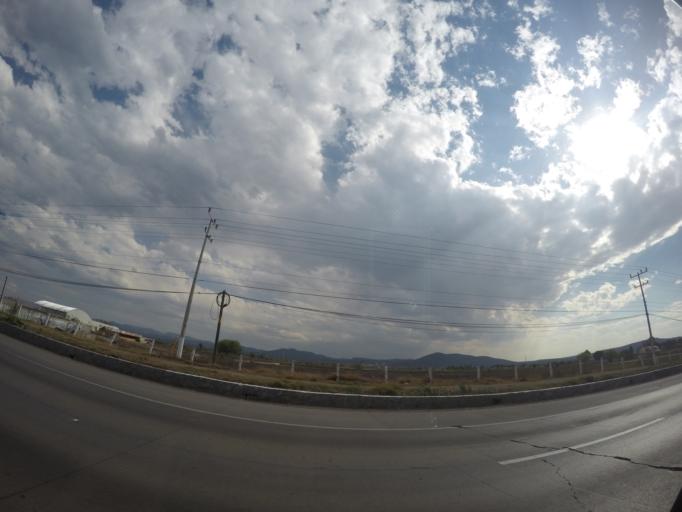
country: MX
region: Queretaro
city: Pedro Escobedo
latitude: 20.5013
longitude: -100.1384
